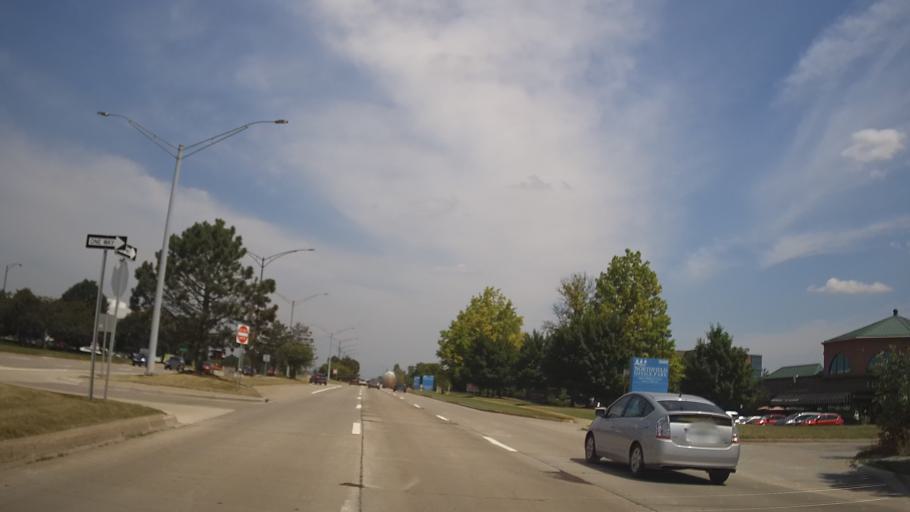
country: US
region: Michigan
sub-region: Oakland County
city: Troy
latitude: 42.6005
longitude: -83.1690
